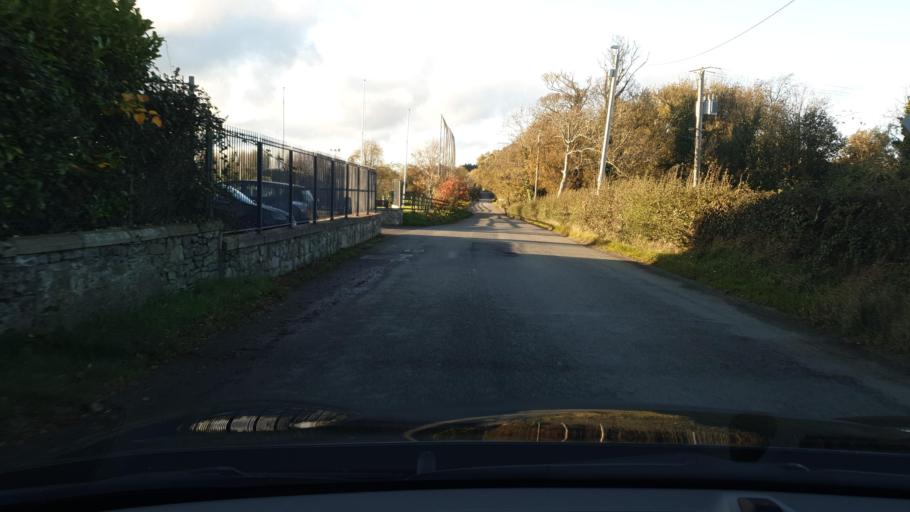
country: IE
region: Leinster
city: Balrothery
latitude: 53.5882
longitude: -6.1936
